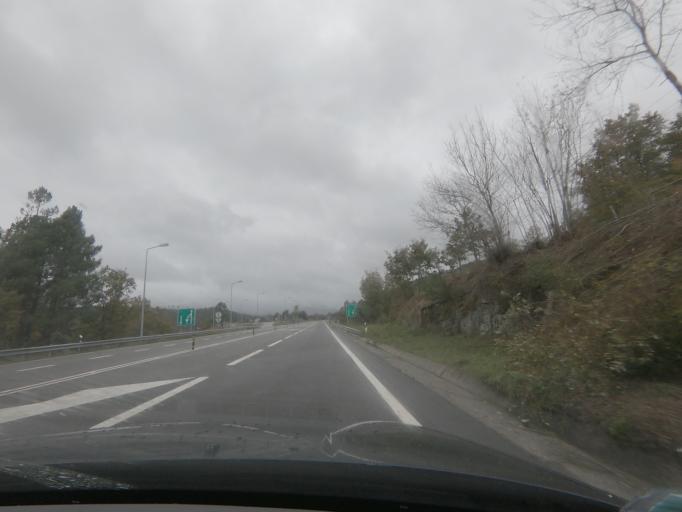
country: PT
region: Vila Real
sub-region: Vila Real
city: Vila Real
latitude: 41.2852
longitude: -7.8129
